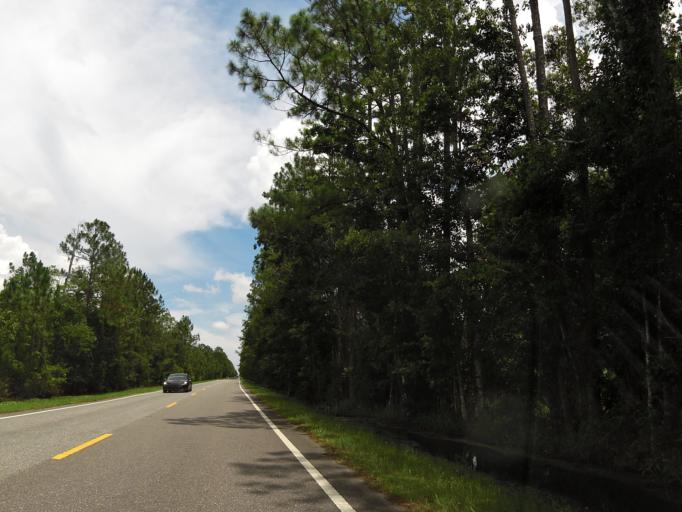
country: US
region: Florida
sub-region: Flagler County
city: Palm Coast
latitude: 29.6544
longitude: -81.3489
